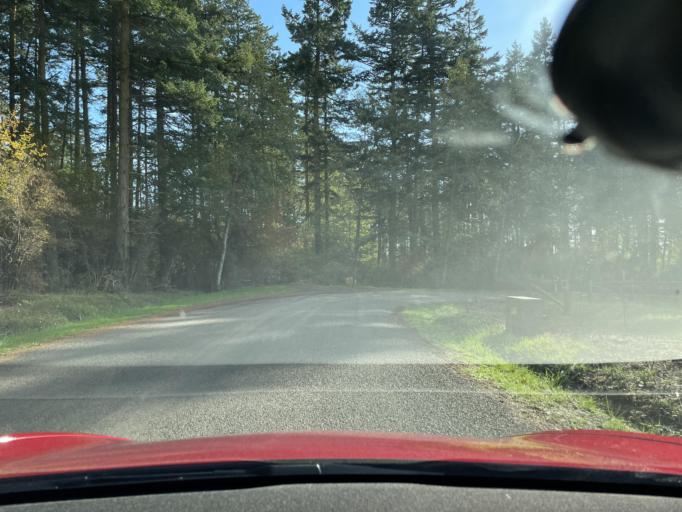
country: US
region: Washington
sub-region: San Juan County
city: Friday Harbor
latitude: 48.4785
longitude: -123.0448
